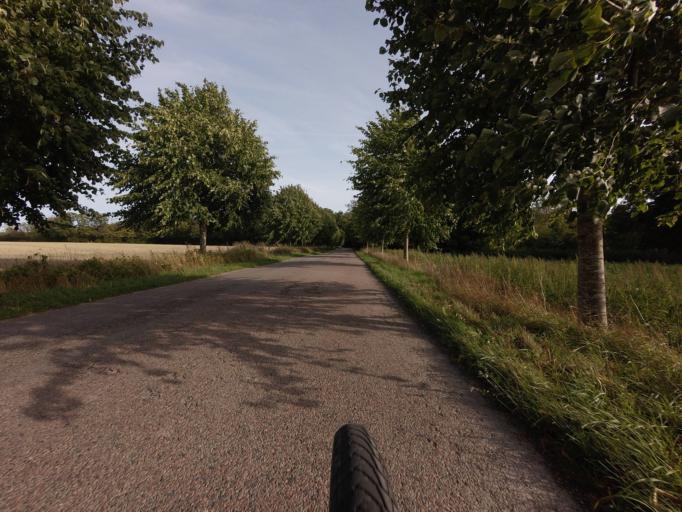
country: DK
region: Zealand
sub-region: Faxe Kommune
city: Fakse Ladeplads
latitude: 55.2442
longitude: 12.2321
